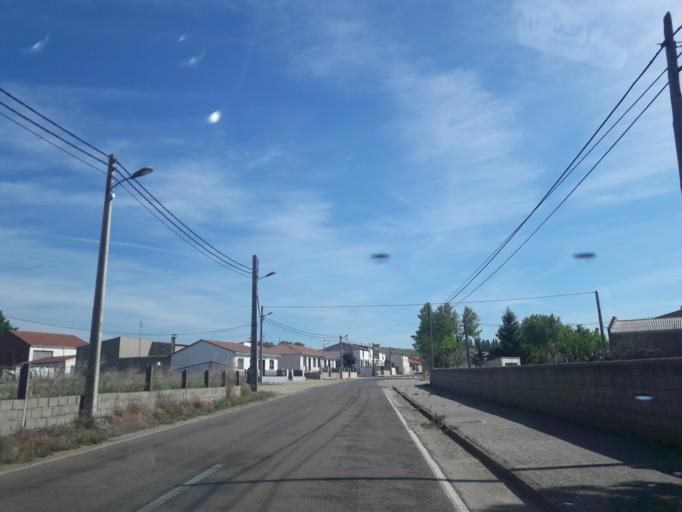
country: ES
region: Castille and Leon
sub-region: Provincia de Salamanca
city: Villoruela
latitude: 41.0048
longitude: -5.3975
